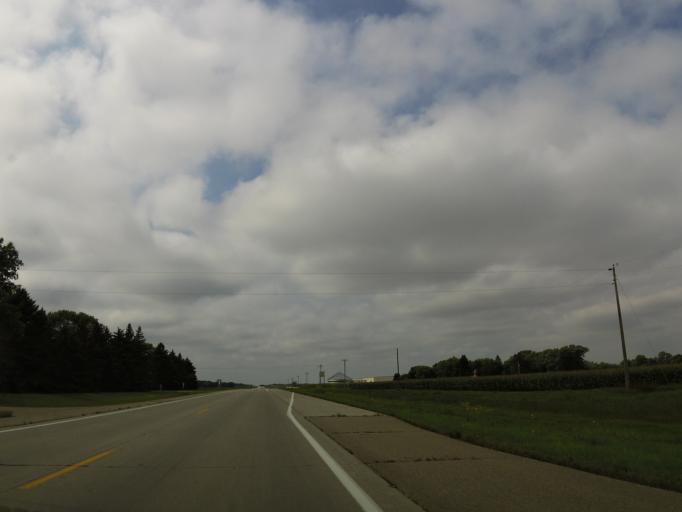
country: US
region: Minnesota
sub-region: Chippewa County
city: Montevideo
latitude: 44.9352
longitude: -95.7641
